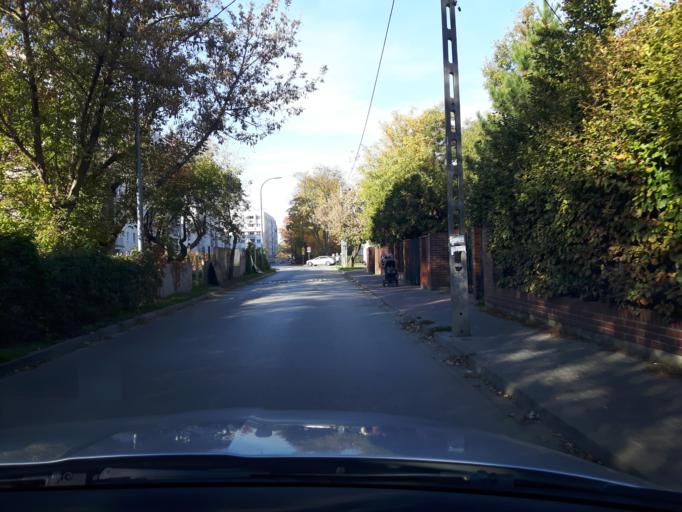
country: PL
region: Masovian Voivodeship
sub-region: Warszawa
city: Bemowo
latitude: 52.2316
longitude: 20.9342
